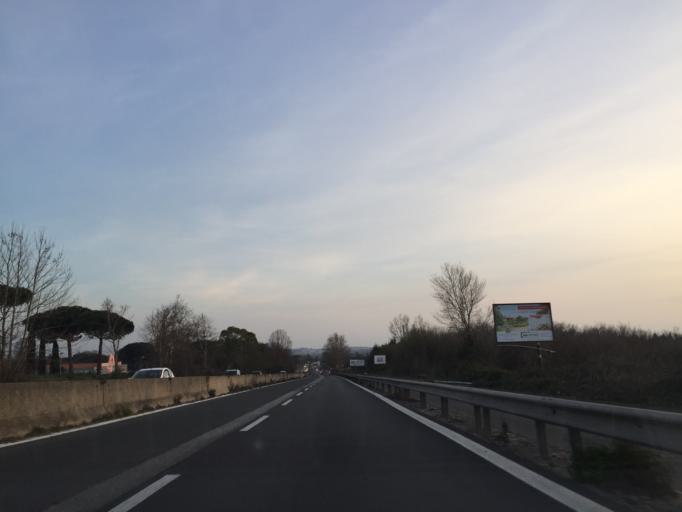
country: IT
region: Latium
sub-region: Citta metropolitana di Roma Capitale
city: Le Rughe
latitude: 42.0689
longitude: 12.3725
